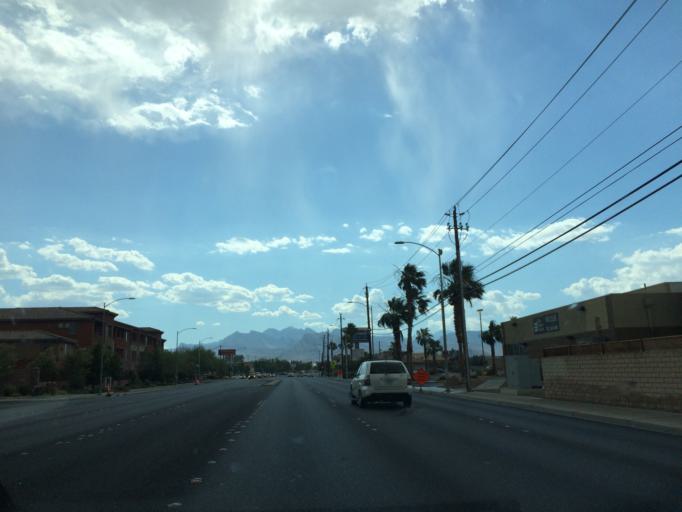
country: US
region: Nevada
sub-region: Clark County
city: Las Vegas
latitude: 36.2169
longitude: -115.2228
